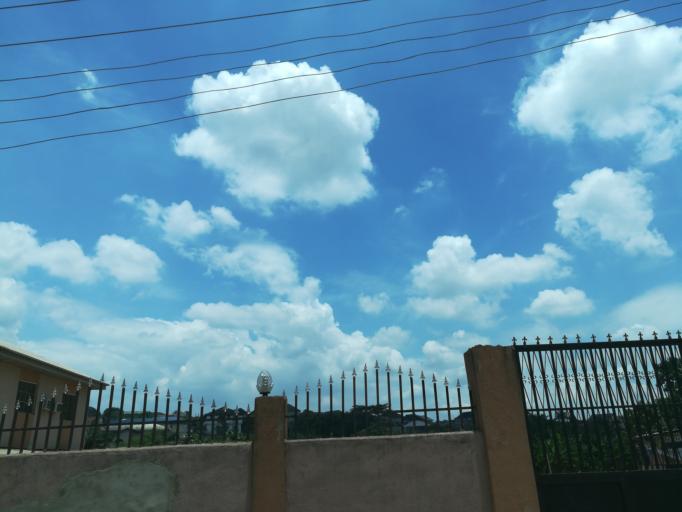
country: NG
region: Lagos
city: Ebute Ikorodu
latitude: 6.6032
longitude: 3.4952
